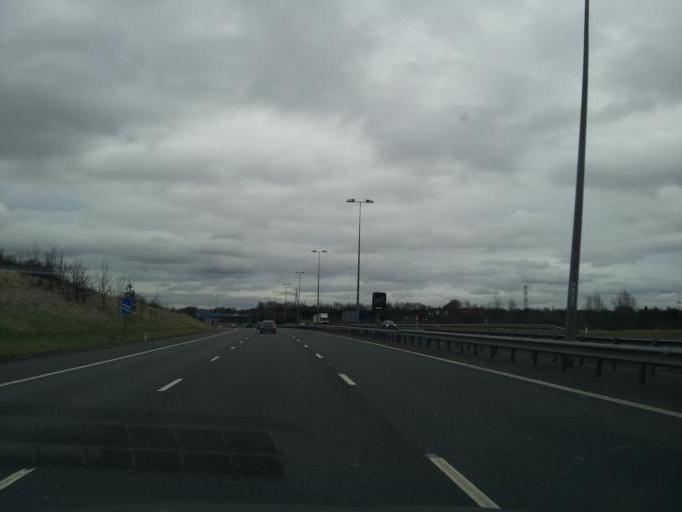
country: GB
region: England
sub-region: Staffordshire
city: Norton Canes
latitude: 52.6628
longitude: -1.9790
